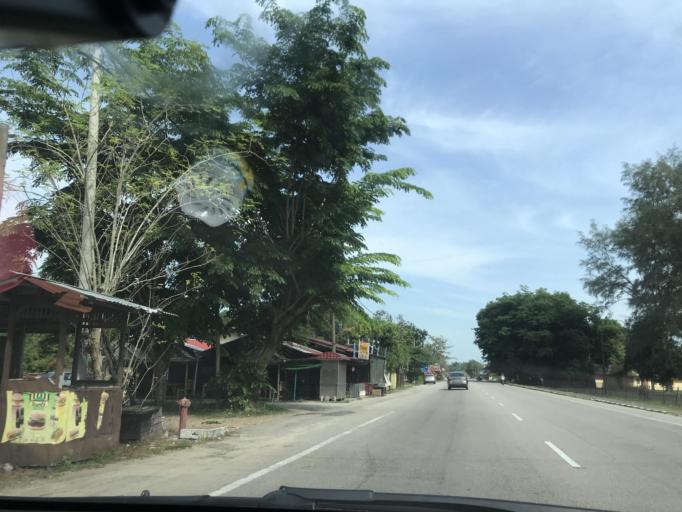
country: MY
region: Kelantan
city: Tumpat
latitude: 6.1904
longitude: 102.1554
